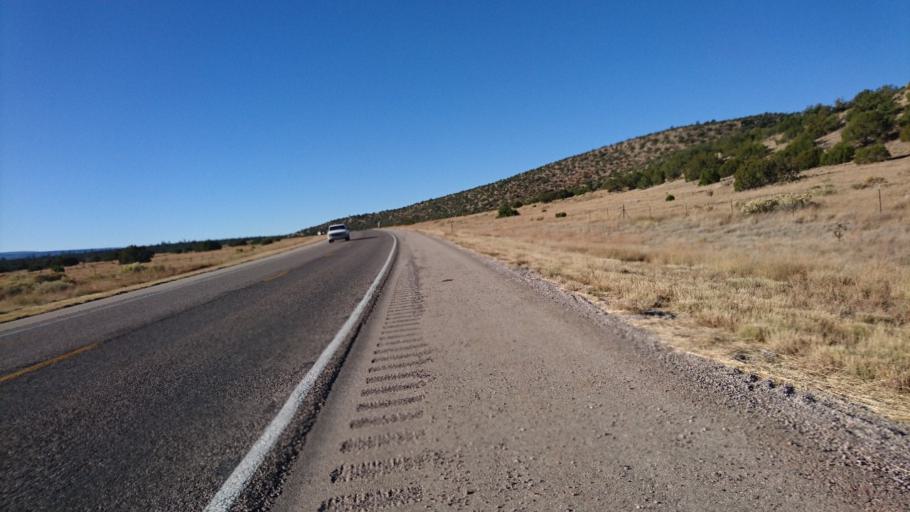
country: US
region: New Mexico
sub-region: Cibola County
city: Grants
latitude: 34.9754
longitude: -107.9115
